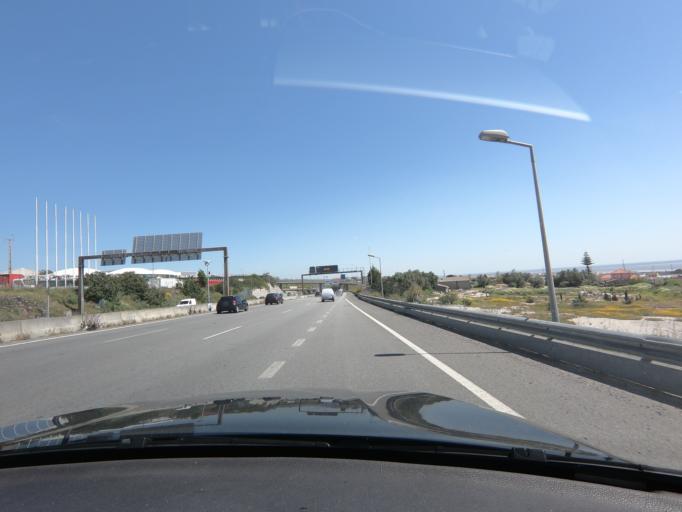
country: PT
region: Lisbon
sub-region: Loures
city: Camarate
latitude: 38.7981
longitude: -9.1399
